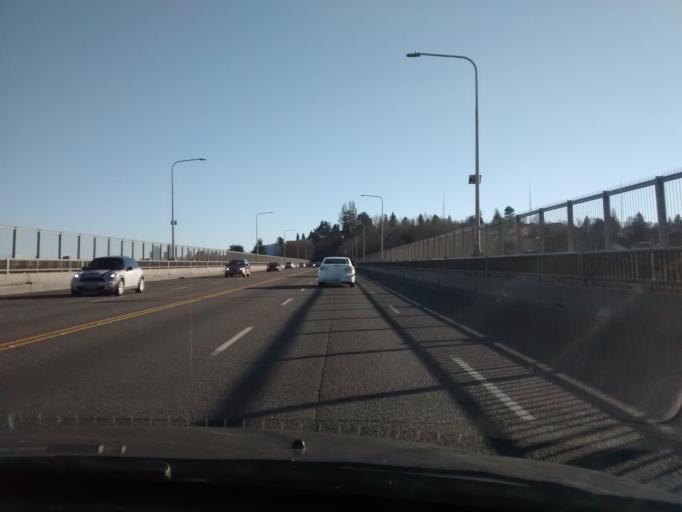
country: US
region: Washington
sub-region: King County
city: Seattle
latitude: 47.6473
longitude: -122.3474
